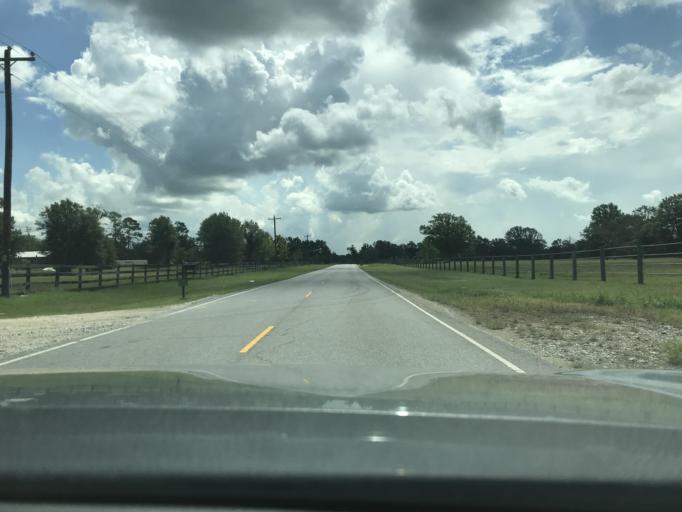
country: US
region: Louisiana
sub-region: Calcasieu Parish
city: Moss Bluff
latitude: 30.3398
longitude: -93.2516
